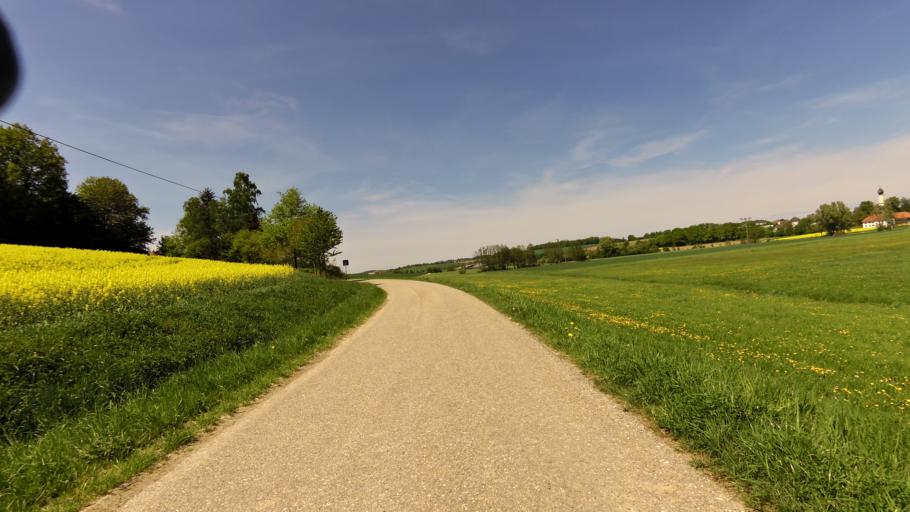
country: DE
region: Bavaria
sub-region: Lower Bavaria
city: Weihmichl
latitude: 48.5798
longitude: 12.0603
